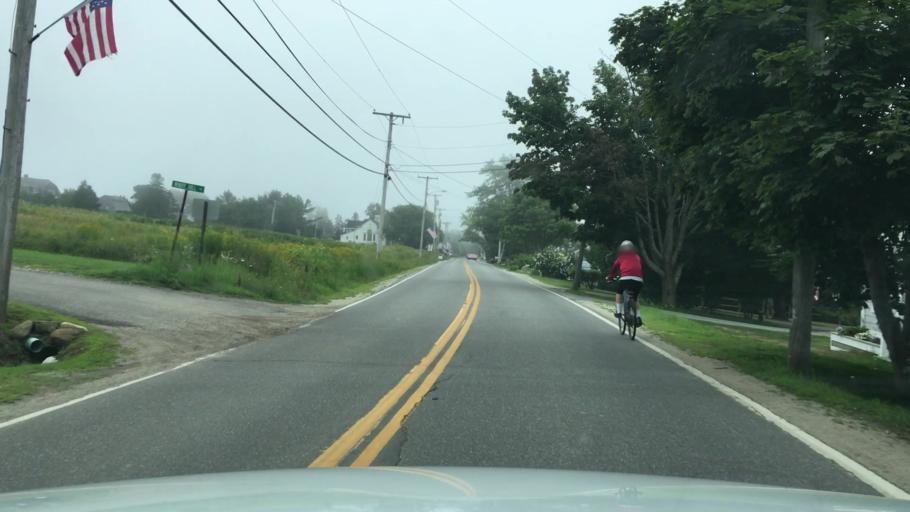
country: US
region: Maine
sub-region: Cumberland County
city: Harpswell Center
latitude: 43.7344
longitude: -69.9957
